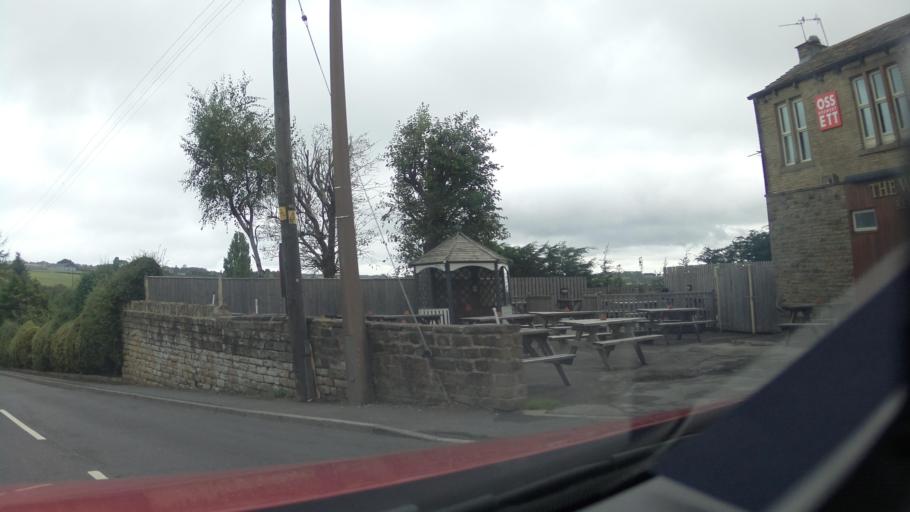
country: GB
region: England
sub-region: Kirklees
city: Clayton West
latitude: 53.6139
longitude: -1.6352
